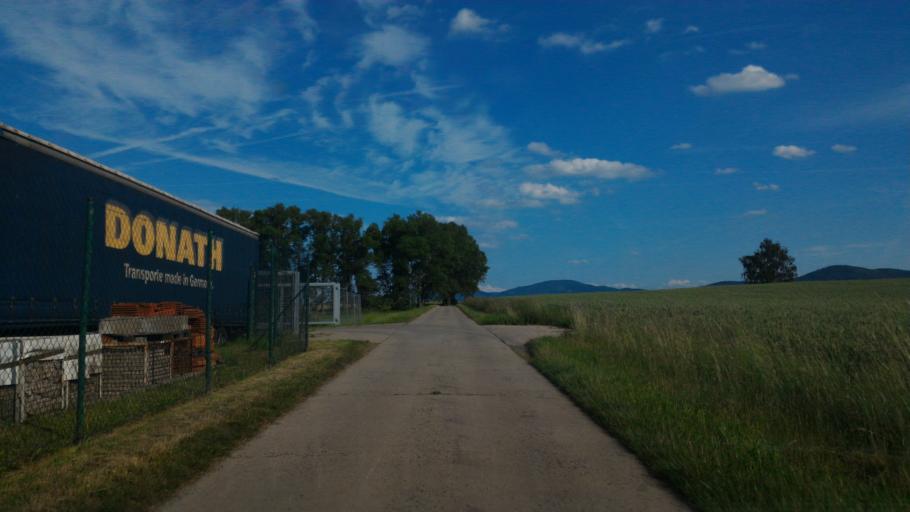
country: DE
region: Saxony
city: Olbersdorf
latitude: 50.8783
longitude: 14.7856
